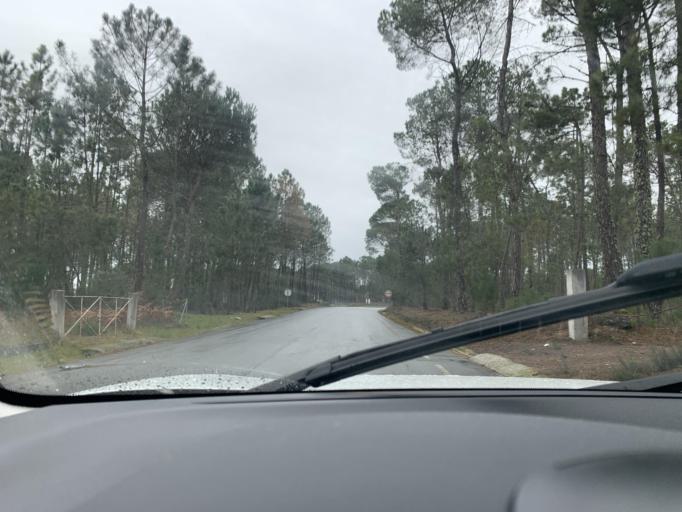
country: PT
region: Viseu
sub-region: Nelas
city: Nelas
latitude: 40.5931
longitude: -7.8326
